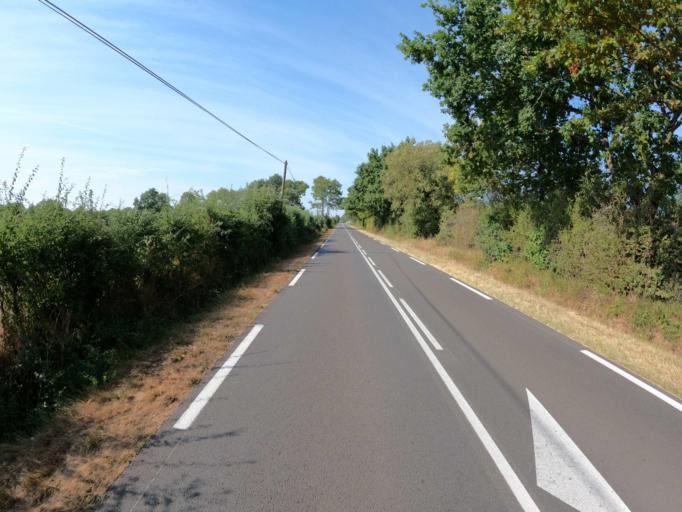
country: FR
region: Pays de la Loire
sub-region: Departement de la Vendee
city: Saint-Christophe-du-Ligneron
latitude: 46.8317
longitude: -1.7572
